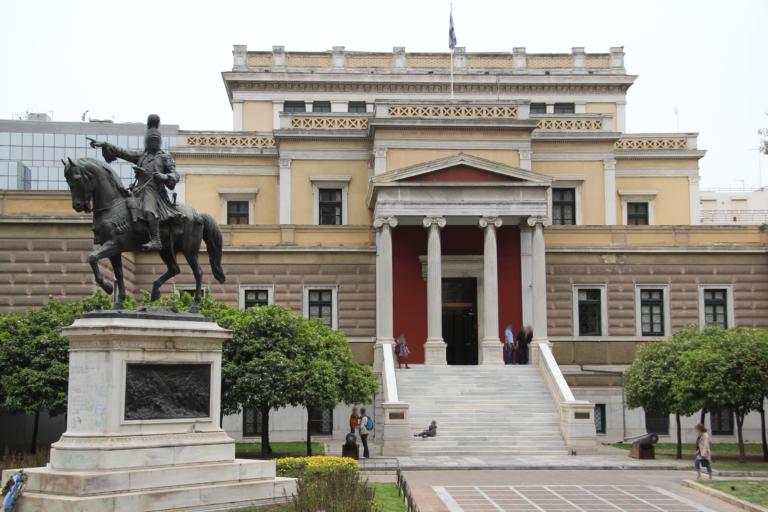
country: GR
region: Attica
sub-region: Nomarchia Athinas
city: Athens
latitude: 37.9777
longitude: 23.7328
